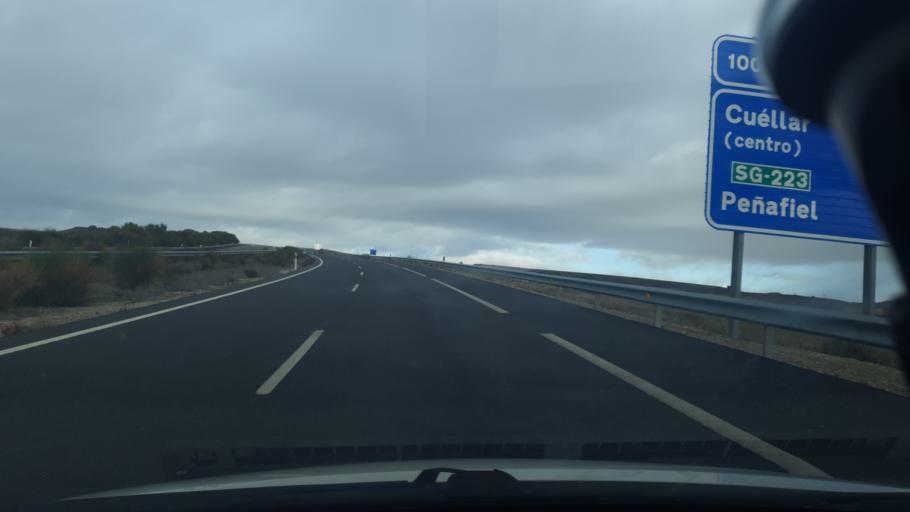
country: ES
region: Castille and Leon
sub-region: Provincia de Segovia
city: Cuellar
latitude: 41.3942
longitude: -4.2914
